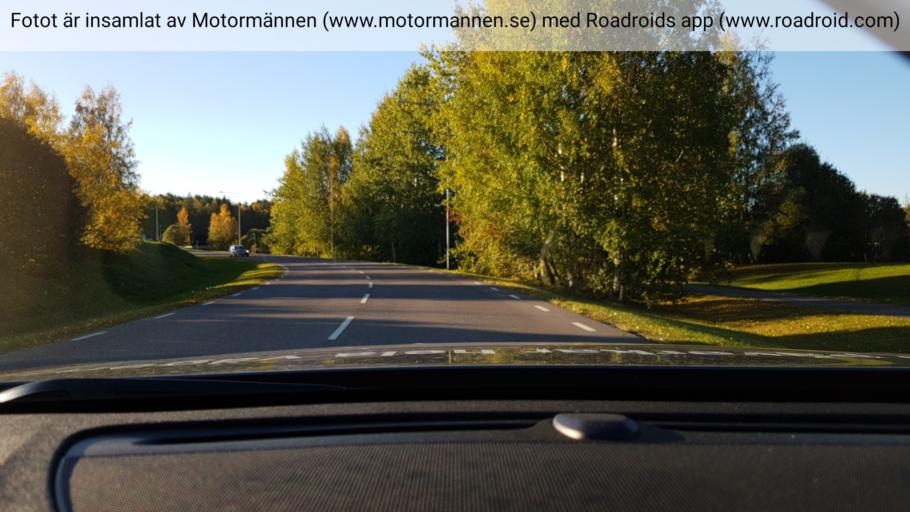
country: SE
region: Norrbotten
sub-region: Lulea Kommun
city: Sodra Sunderbyn
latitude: 65.6553
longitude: 21.9460
